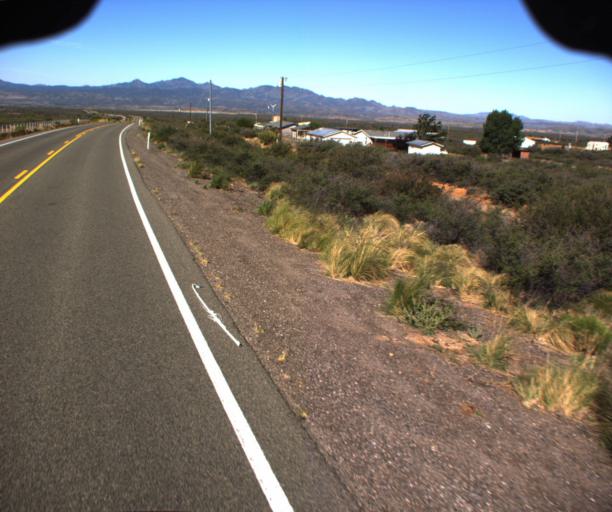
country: US
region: Arizona
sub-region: Yavapai County
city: Prescott
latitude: 34.4137
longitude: -112.6047
